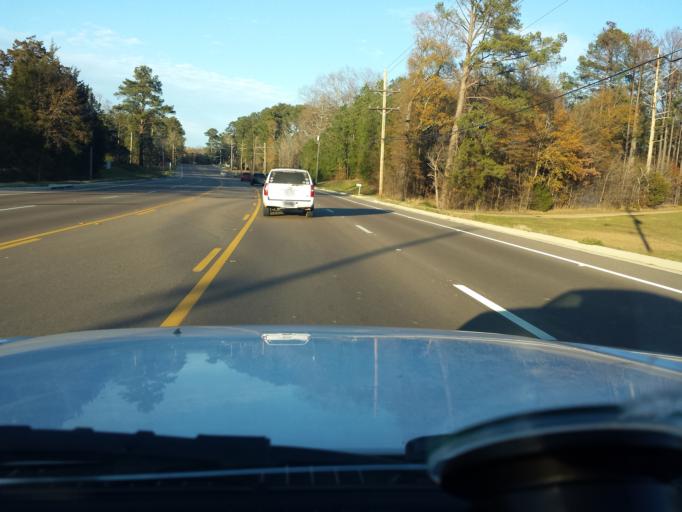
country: US
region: Mississippi
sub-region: Rankin County
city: Flowood
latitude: 32.3595
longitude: -90.0582
